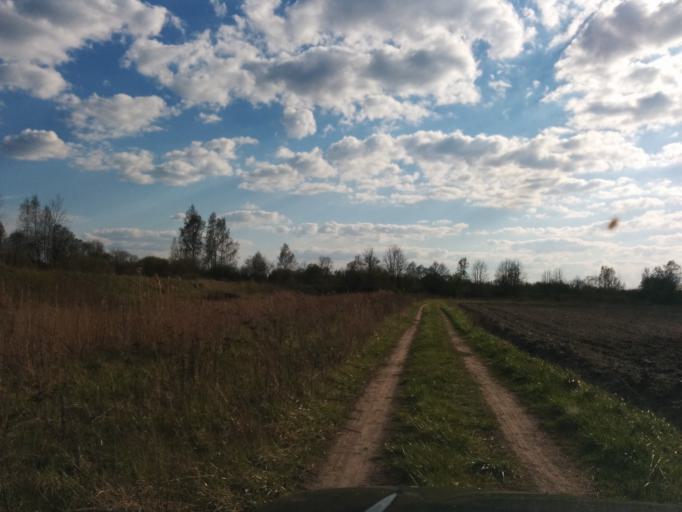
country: LV
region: Jelgava
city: Jelgava
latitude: 56.6765
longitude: 23.6875
